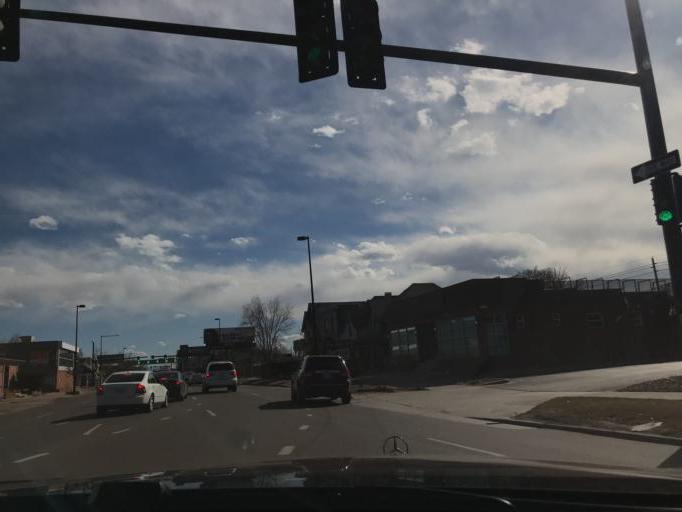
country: US
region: Colorado
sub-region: Denver County
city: Denver
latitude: 39.7286
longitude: -105.0002
